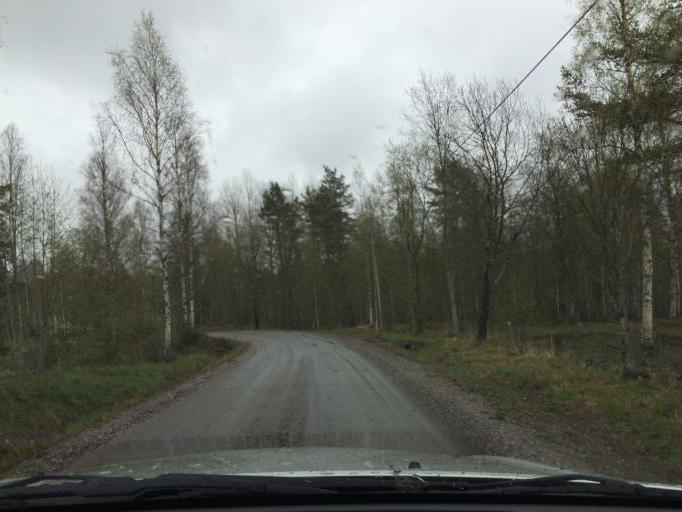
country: SE
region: Dalarna
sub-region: Ludvika Kommun
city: Abborrberget
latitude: 60.0408
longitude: 14.6978
